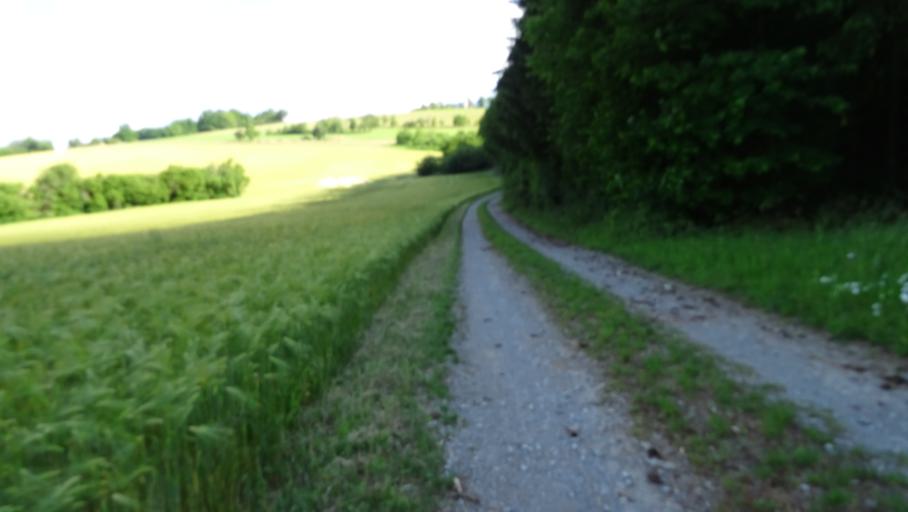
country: DE
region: Baden-Wuerttemberg
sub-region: Karlsruhe Region
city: Seckach
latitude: 49.4350
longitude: 9.3573
